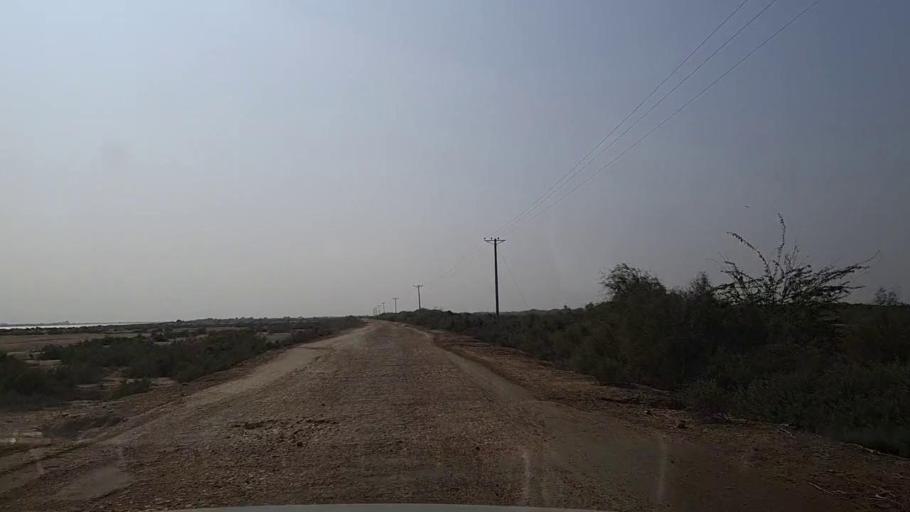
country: PK
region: Sindh
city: Mirpur Sakro
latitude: 24.5387
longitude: 67.5997
